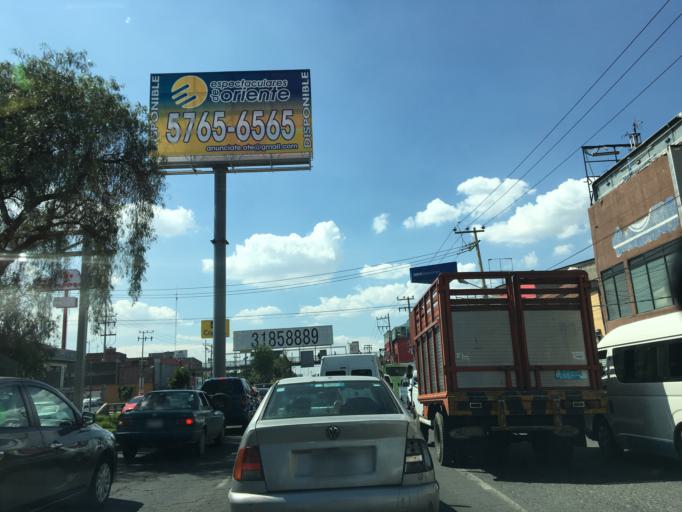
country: MX
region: Mexico
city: Los Reyes La Paz
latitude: 19.3574
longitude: -98.9877
